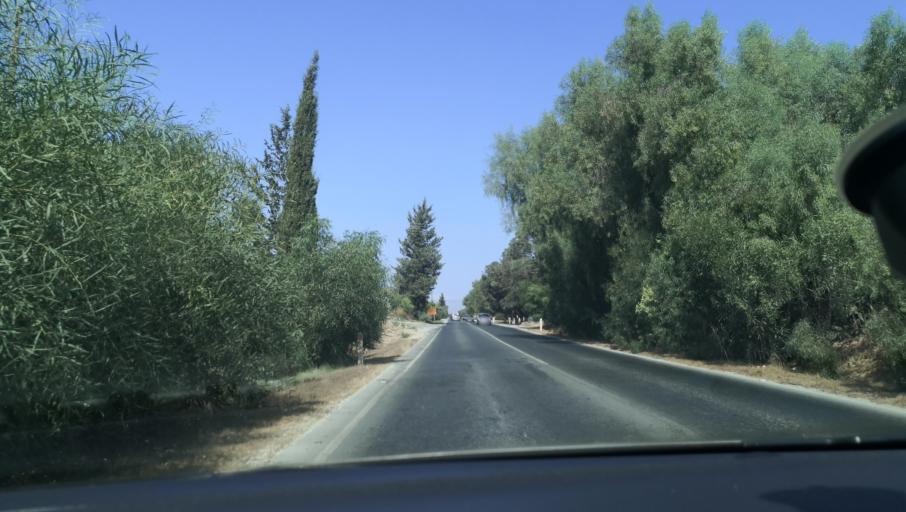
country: CY
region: Lefkosia
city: Kato Deftera
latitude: 35.1024
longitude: 33.2865
